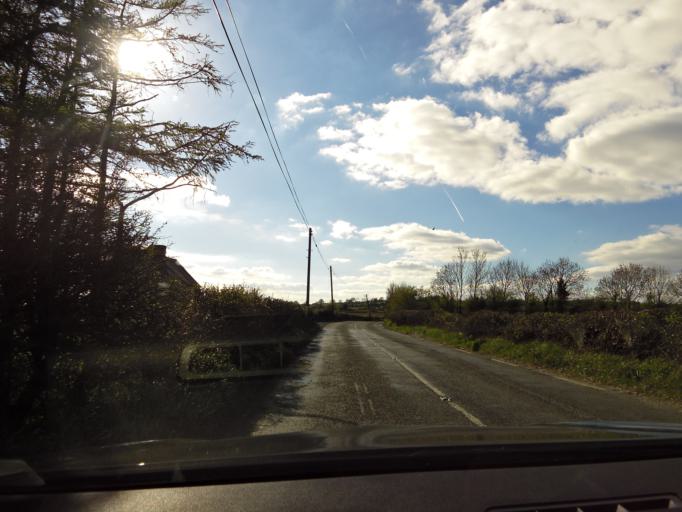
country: IE
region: Connaught
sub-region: County Galway
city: Portumna
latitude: 53.1110
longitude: -8.1055
